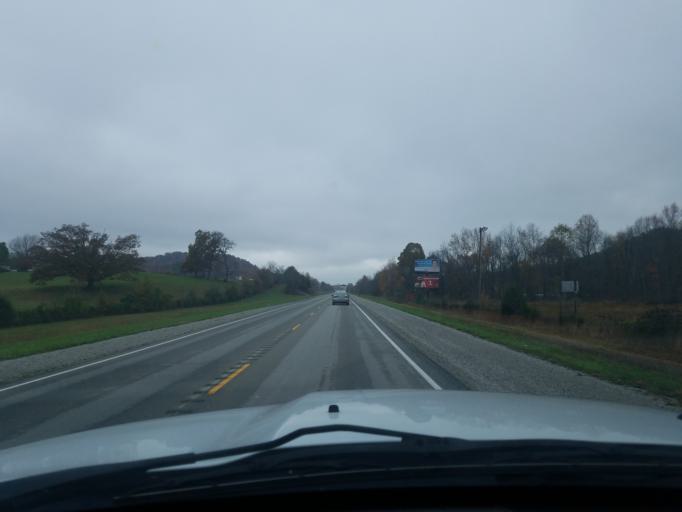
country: US
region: Kentucky
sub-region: Marion County
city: Lebanon
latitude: 37.5192
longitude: -85.2991
